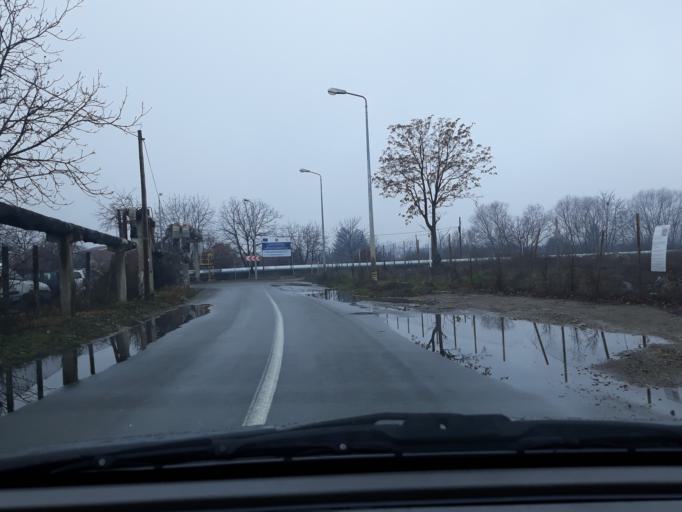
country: RO
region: Bihor
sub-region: Comuna Sanmartin
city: Sanmartin
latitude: 47.0376
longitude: 21.9607
